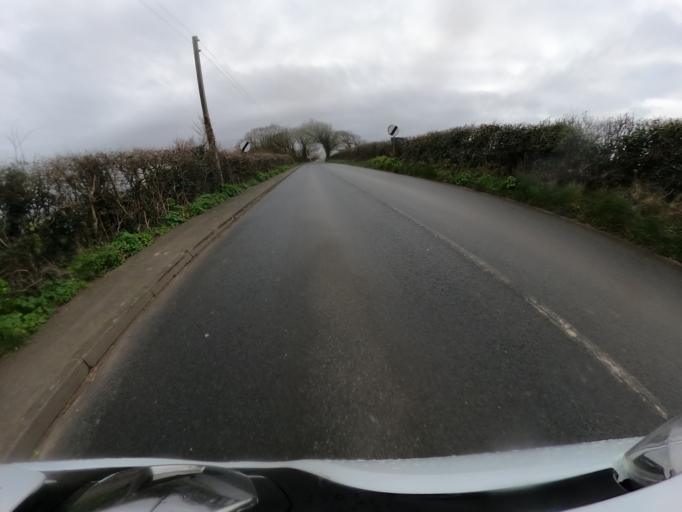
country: IM
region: Ramsey
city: Ramsey
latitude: 54.3638
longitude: -4.4520
